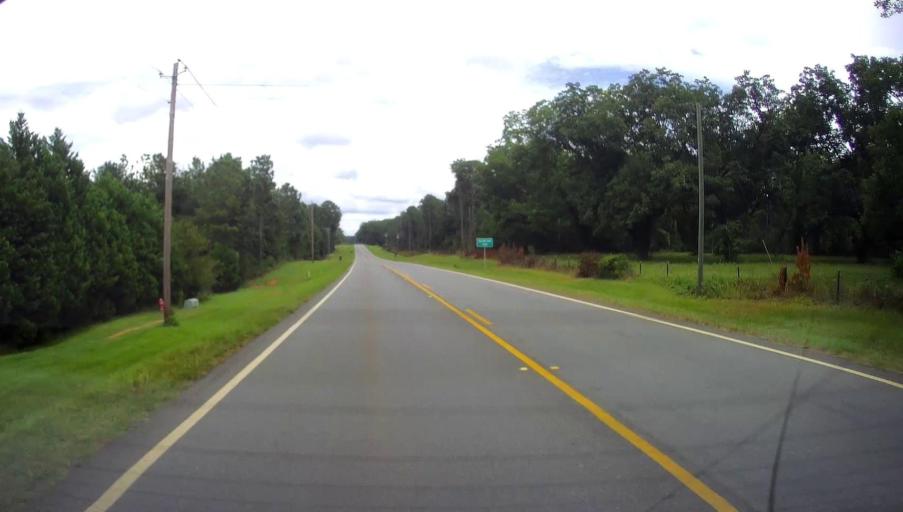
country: US
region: Georgia
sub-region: Schley County
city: Ellaville
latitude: 32.2571
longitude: -84.2668
